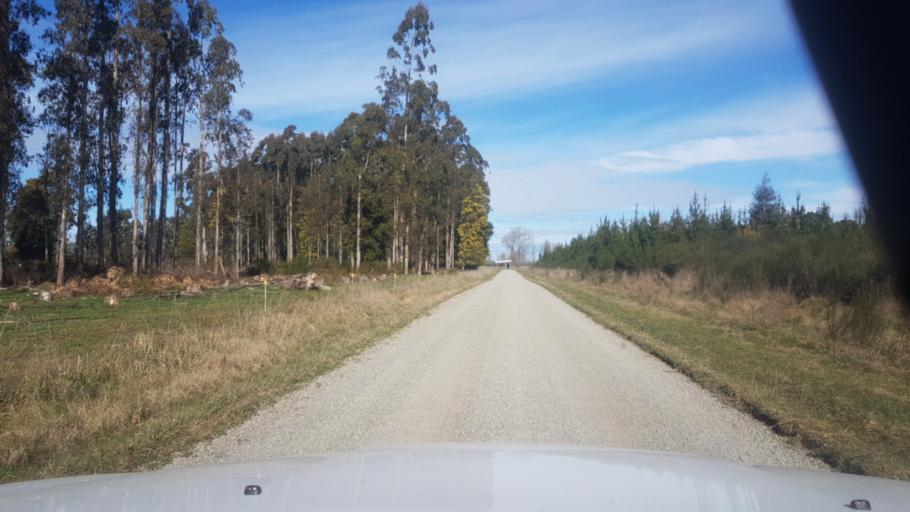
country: NZ
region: Canterbury
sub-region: Timaru District
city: Pleasant Point
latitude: -44.1415
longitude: 171.2751
